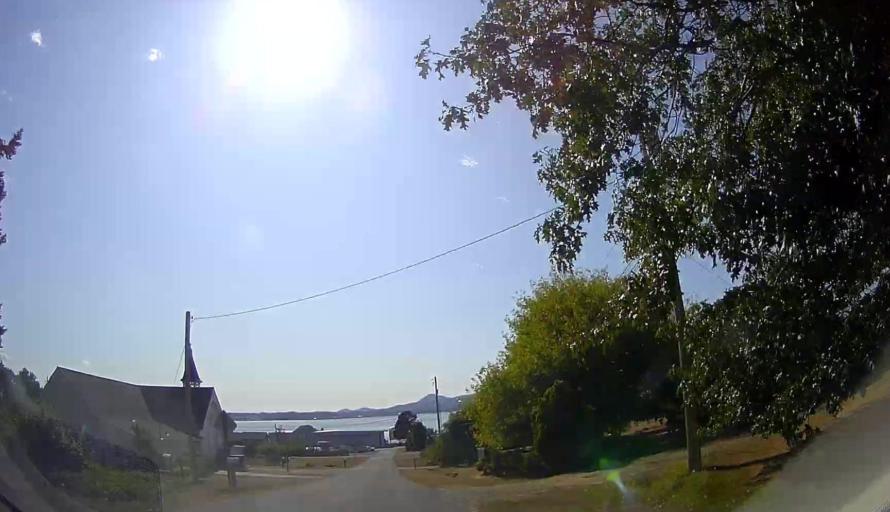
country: US
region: Washington
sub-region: Skagit County
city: Anacortes
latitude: 48.4852
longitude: -122.4753
